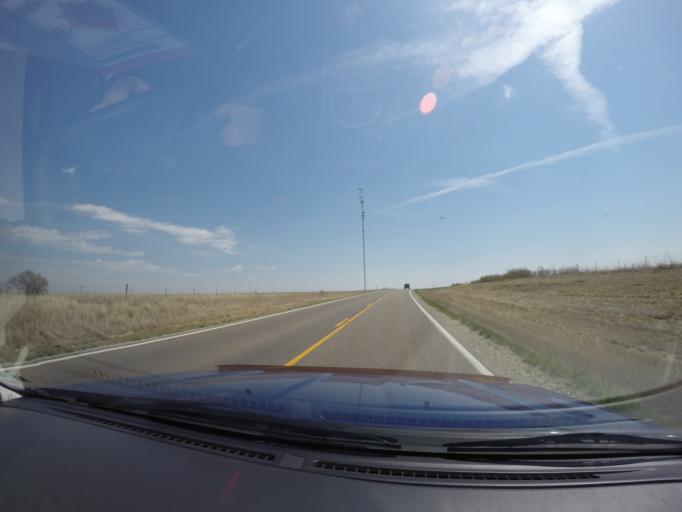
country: US
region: Kansas
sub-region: Morris County
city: Council Grove
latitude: 38.8655
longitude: -96.5079
